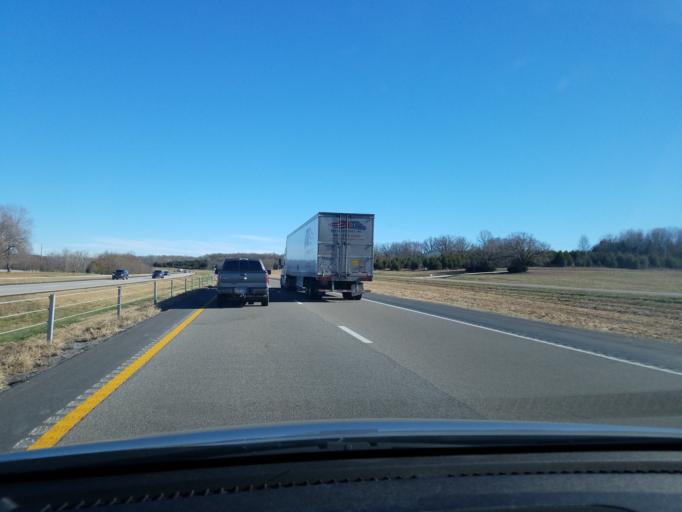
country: US
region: Missouri
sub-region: Webster County
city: Marshfield
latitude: 37.3026
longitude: -92.9923
